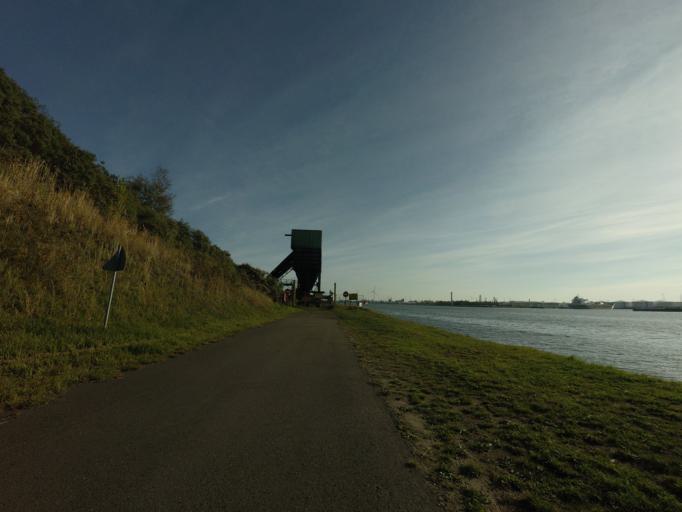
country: BE
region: Flanders
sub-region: Provincie Antwerpen
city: Stabroek
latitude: 51.3324
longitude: 4.3068
